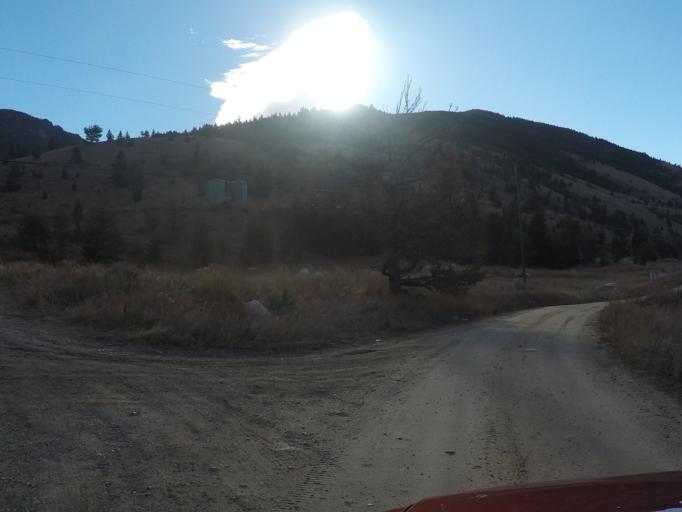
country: US
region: Montana
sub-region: Carbon County
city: Red Lodge
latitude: 45.1150
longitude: -109.2981
